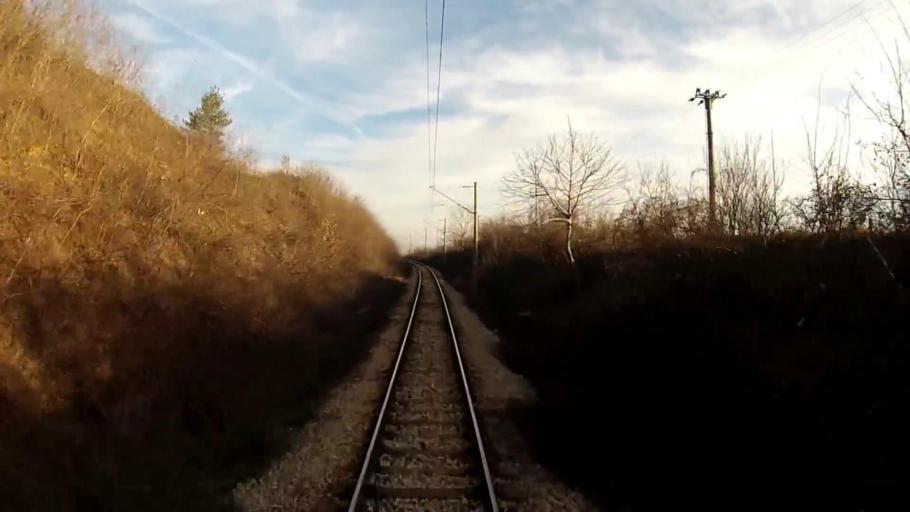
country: BG
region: Plovdiv
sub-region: Obshtina Karlovo
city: Klisura
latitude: 42.7174
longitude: 24.5991
